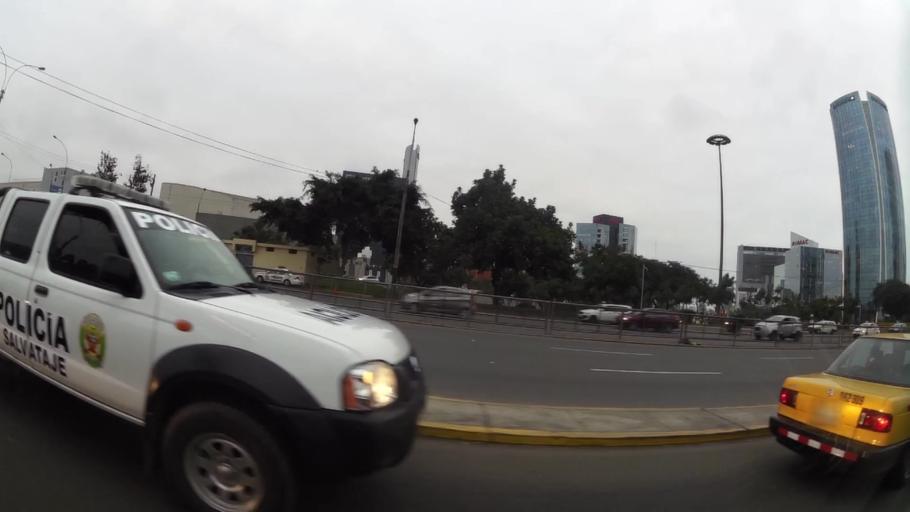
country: PE
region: Lima
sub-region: Lima
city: San Luis
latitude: -12.0906
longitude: -77.0222
